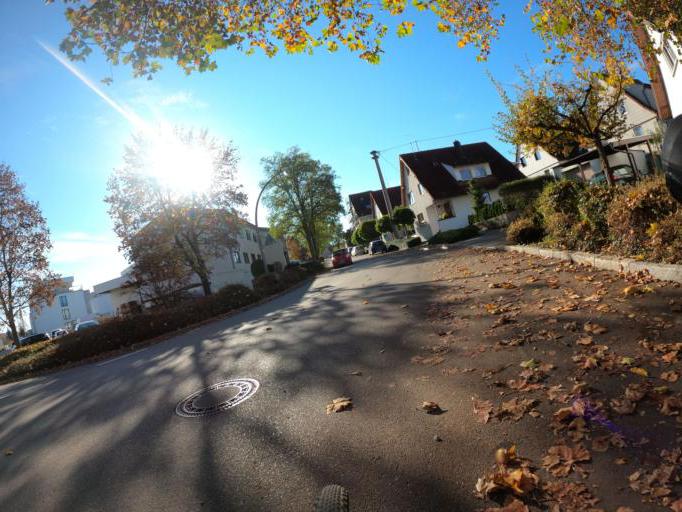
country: DE
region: Baden-Wuerttemberg
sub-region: Regierungsbezirk Stuttgart
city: Magstadt
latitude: 48.7382
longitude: 8.9657
